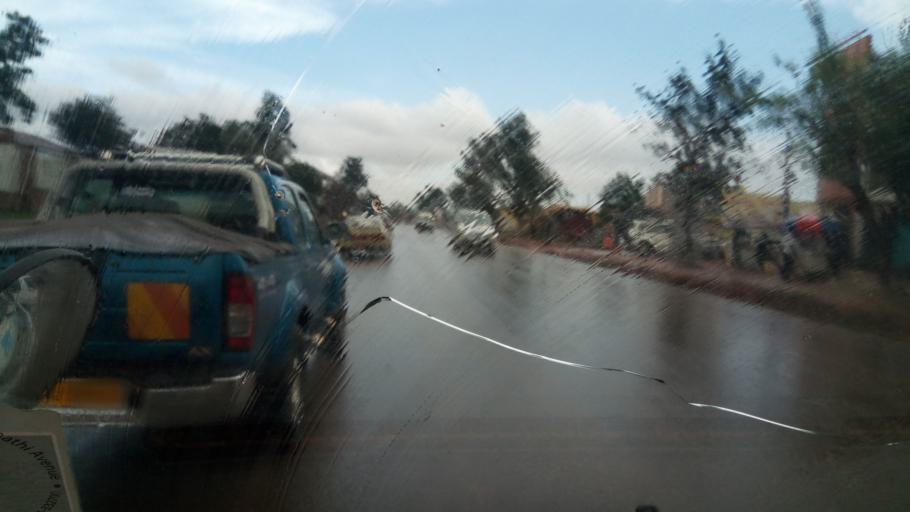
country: UG
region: Central Region
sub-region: Wakiso District
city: Wakiso
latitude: 0.3855
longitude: 32.5154
